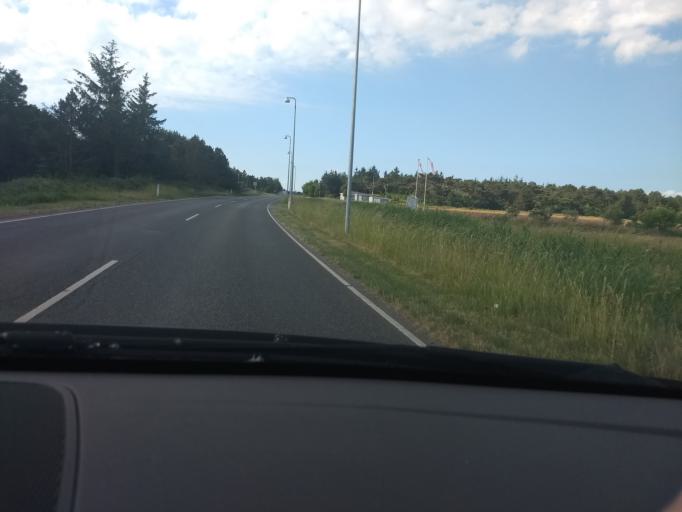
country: DE
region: Schleswig-Holstein
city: List
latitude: 55.1276
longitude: 8.5503
